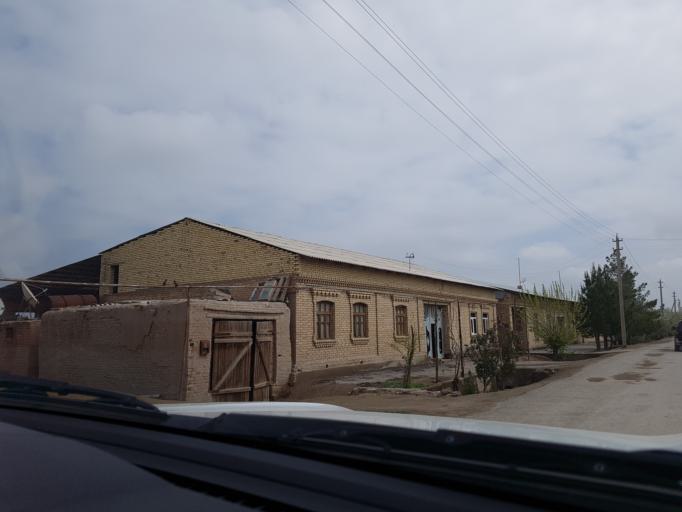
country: TM
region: Lebap
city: Turkmenabat
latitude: 38.9716
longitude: 63.6908
